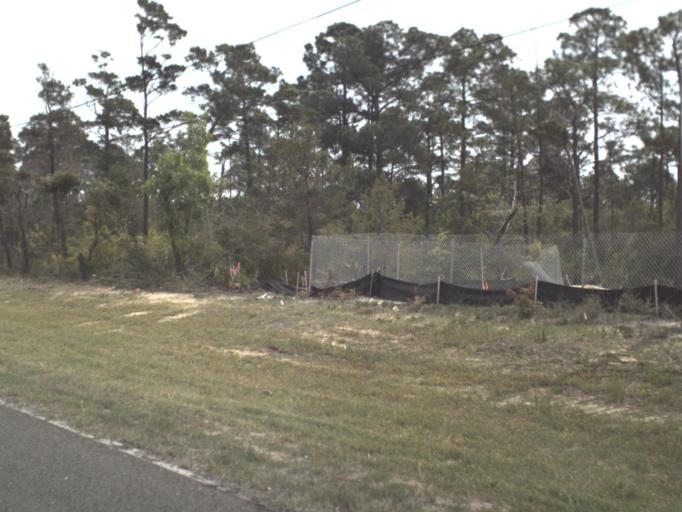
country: US
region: Florida
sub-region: Santa Rosa County
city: Holley
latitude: 30.4019
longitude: -86.9131
